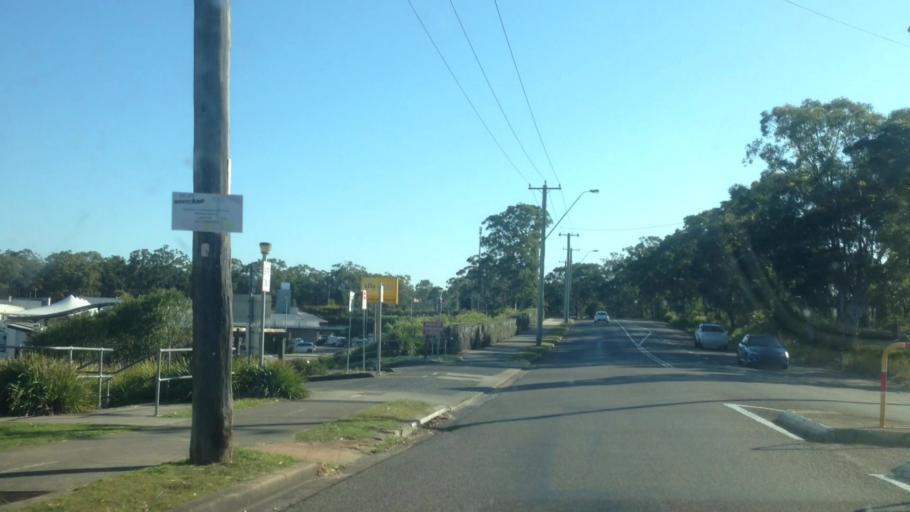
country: AU
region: New South Wales
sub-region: Lake Macquarie Shire
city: Dora Creek
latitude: -33.1095
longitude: 151.5333
